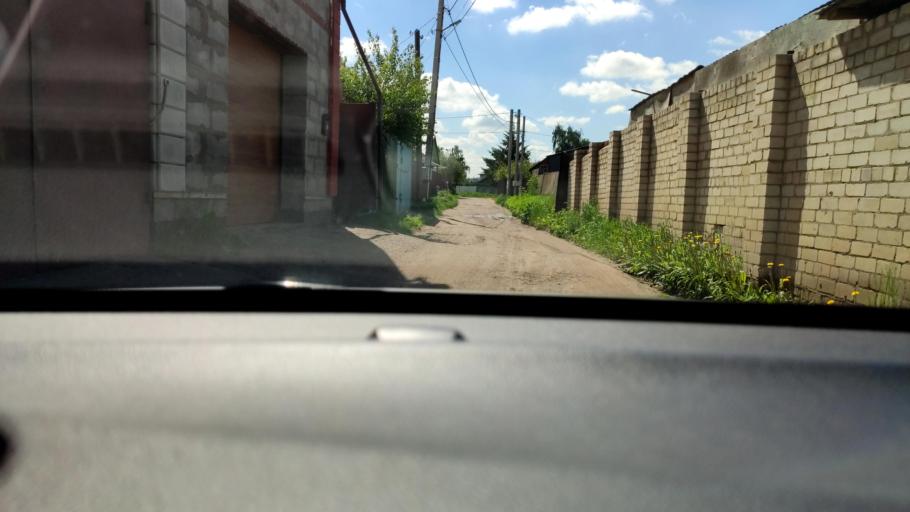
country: RU
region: Tatarstan
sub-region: Gorod Kazan'
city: Kazan
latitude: 55.7754
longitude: 49.1584
